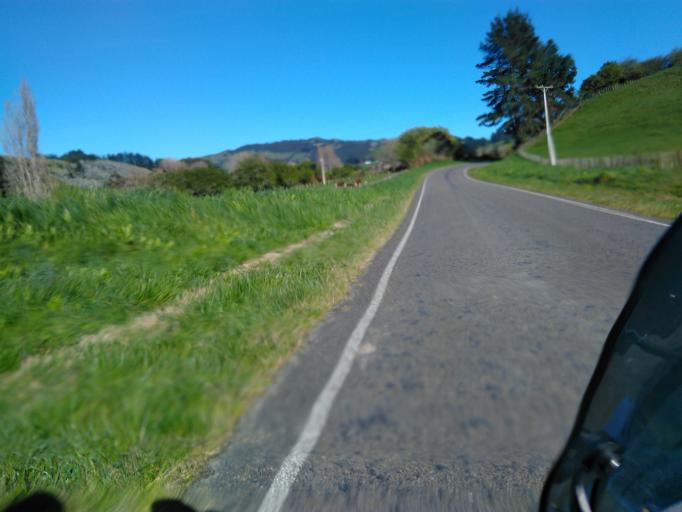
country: NZ
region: Gisborne
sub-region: Gisborne District
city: Gisborne
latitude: -38.4279
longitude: 177.7273
